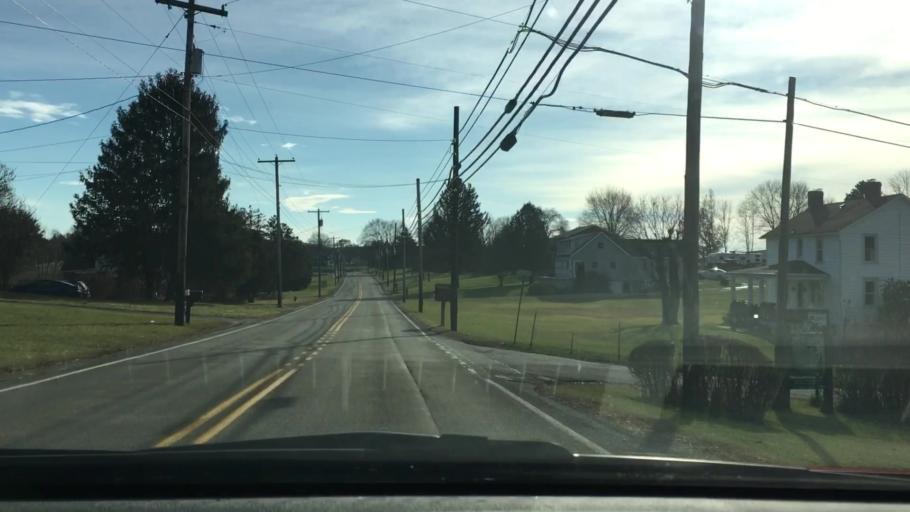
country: US
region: Pennsylvania
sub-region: Westmoreland County
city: West Newton
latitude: 40.1994
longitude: -79.7438
